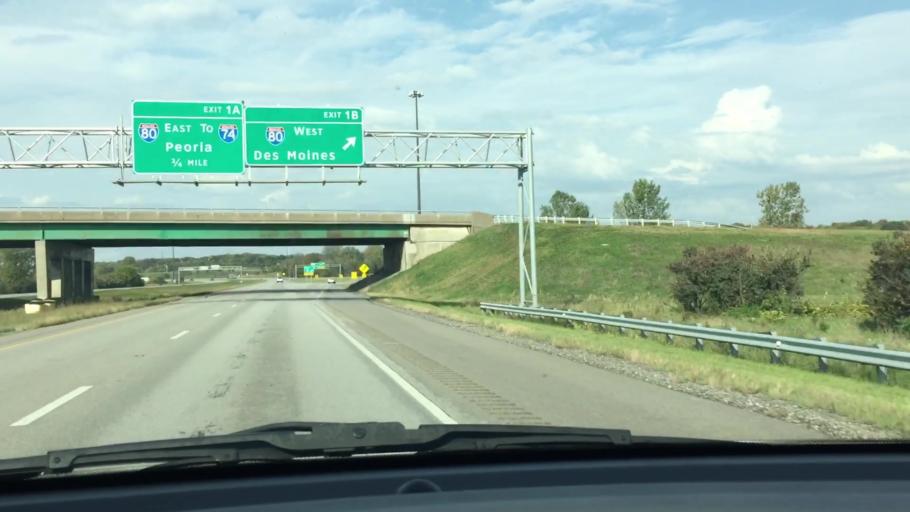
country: US
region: Illinois
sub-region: Henry County
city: Colona
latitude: 41.5361
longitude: -90.3266
